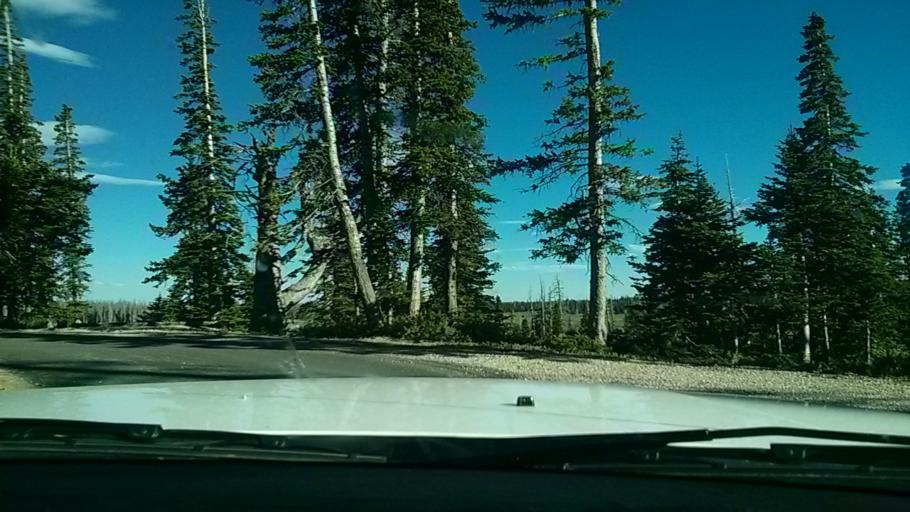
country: US
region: Utah
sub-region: Iron County
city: Parowan
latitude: 37.6098
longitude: -112.8313
